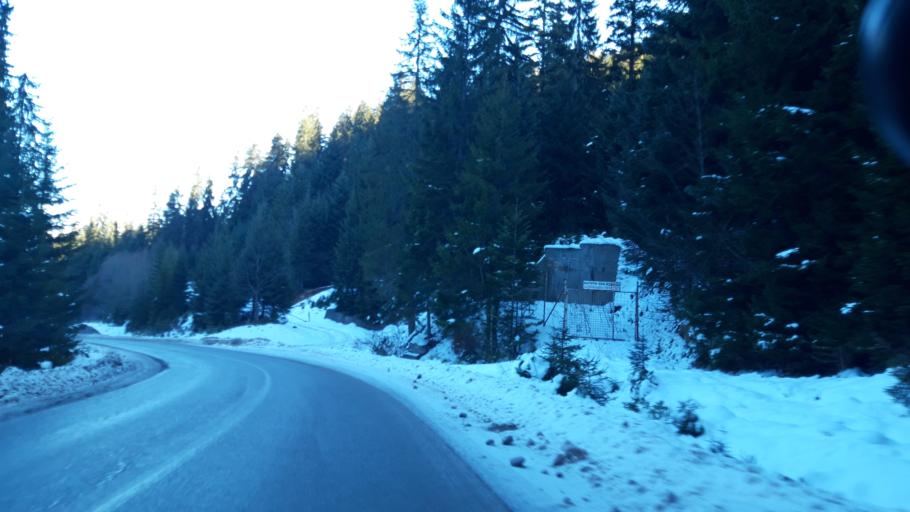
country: BA
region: Republika Srpska
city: Koran
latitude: 43.7754
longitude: 18.5530
